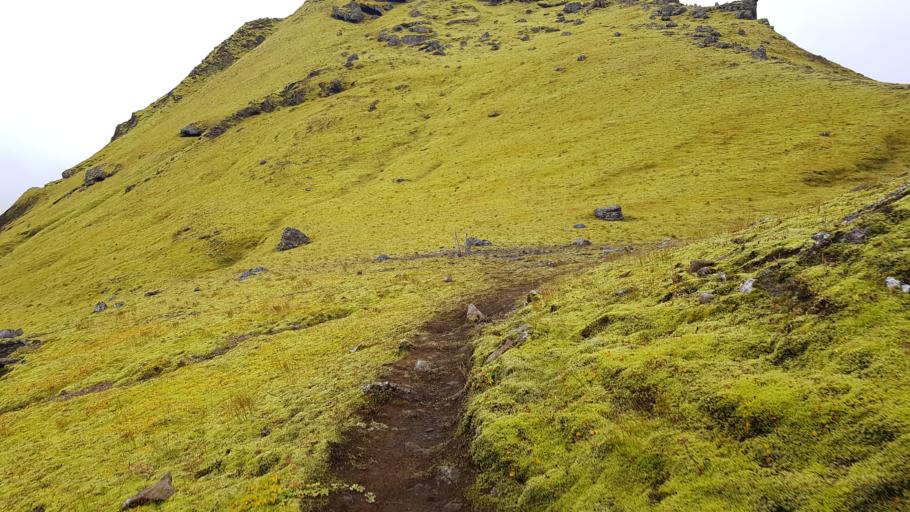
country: IS
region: South
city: Vestmannaeyjar
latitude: 63.5375
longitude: -18.8544
